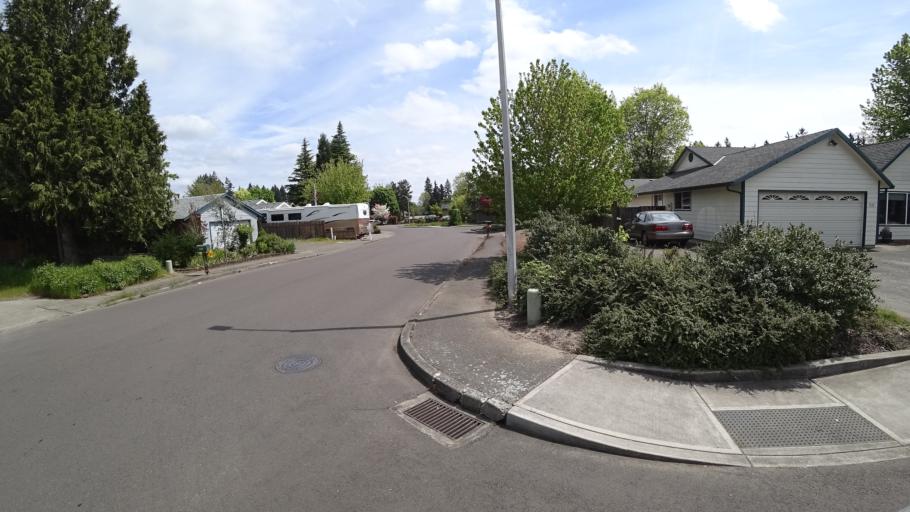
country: US
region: Oregon
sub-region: Washington County
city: Hillsboro
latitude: 45.5382
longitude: -122.9947
